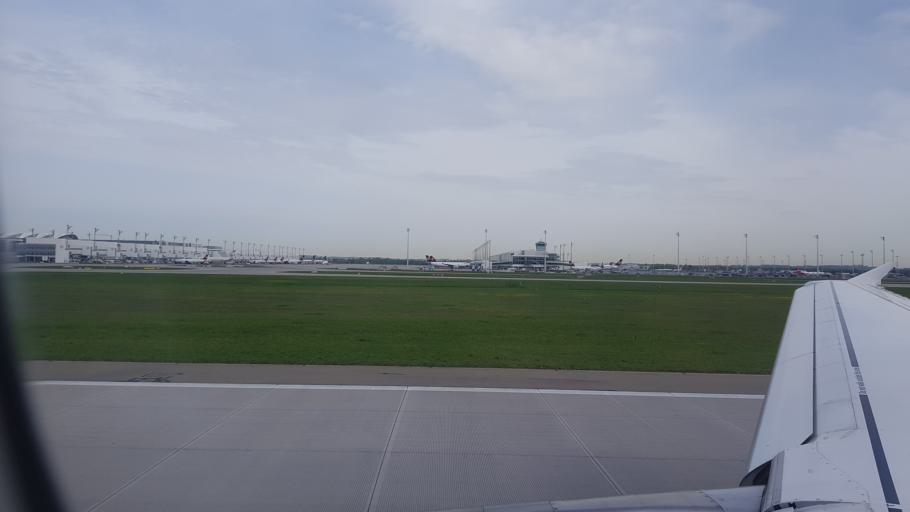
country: DE
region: Bavaria
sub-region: Upper Bavaria
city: Hallbergmoos
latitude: 48.3449
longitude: 11.7991
